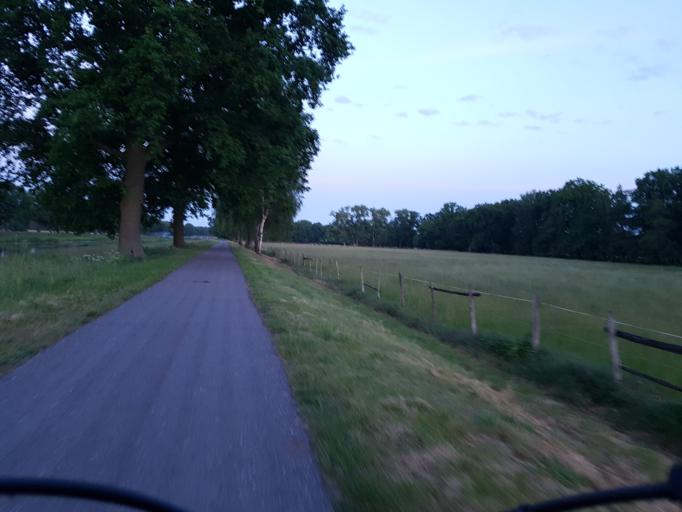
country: DE
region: Brandenburg
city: Schilda
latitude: 51.5791
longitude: 13.3429
